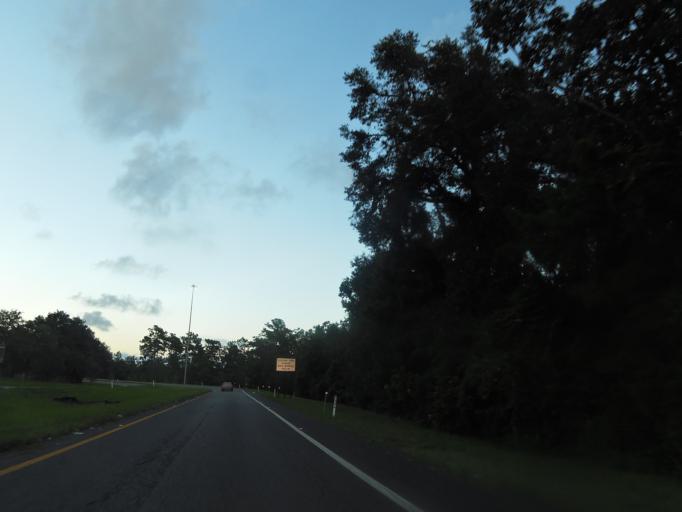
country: US
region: Florida
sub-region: Duval County
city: Jacksonville
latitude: 30.4587
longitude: -81.6789
